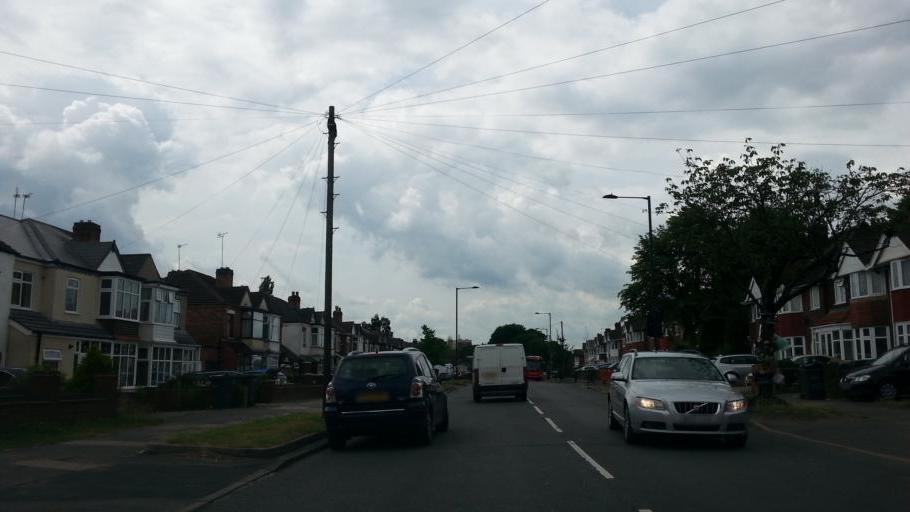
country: GB
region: England
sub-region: City and Borough of Birmingham
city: Acocks Green
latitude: 52.4929
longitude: -1.8089
